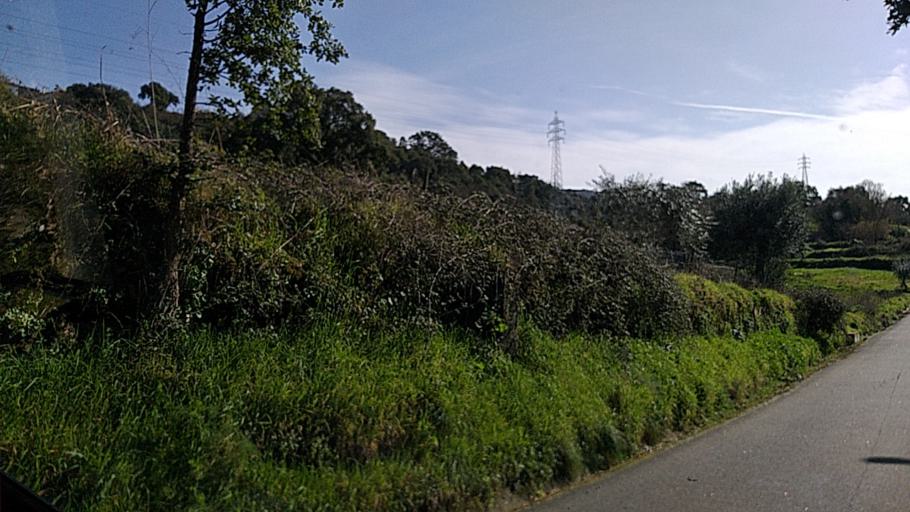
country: PT
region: Guarda
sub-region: Celorico da Beira
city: Celorico da Beira
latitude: 40.6382
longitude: -7.3968
